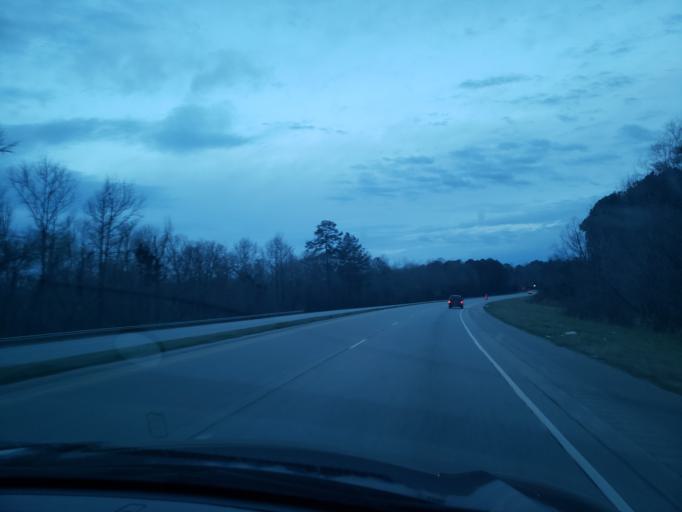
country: US
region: Alabama
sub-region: Lee County
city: Auburn
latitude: 32.6584
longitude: -85.4629
